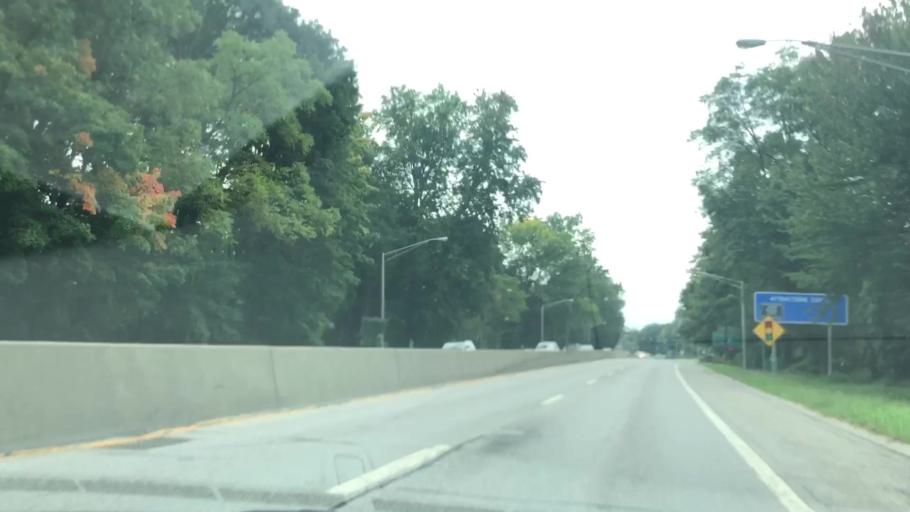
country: US
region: New York
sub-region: Westchester County
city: Hastings-on-Hudson
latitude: 40.9828
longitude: -73.8667
